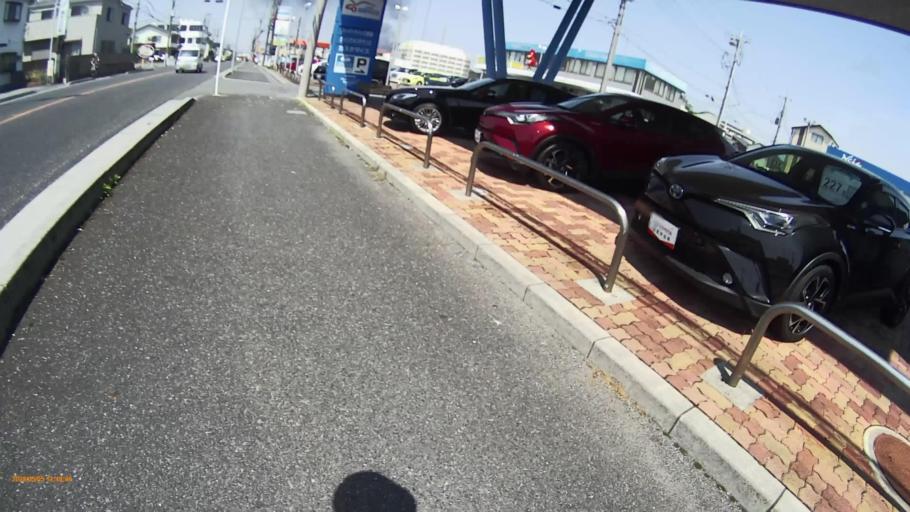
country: JP
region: Saitama
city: Kasukabe
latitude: 35.9506
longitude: 139.7759
